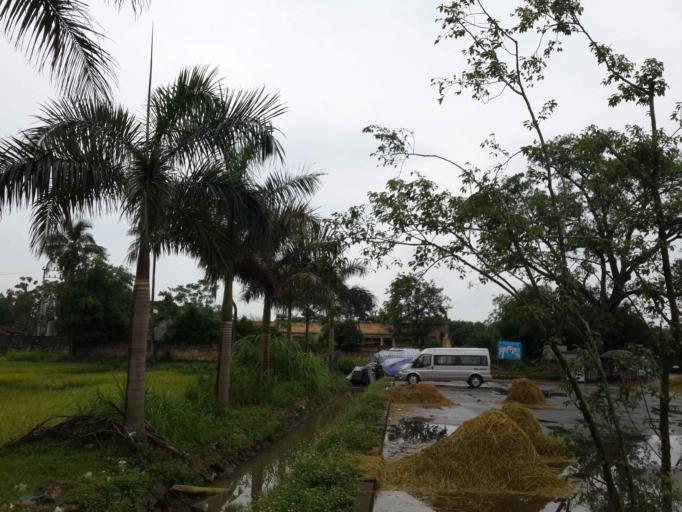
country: VN
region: Ha Noi
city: Son Tay
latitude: 21.1567
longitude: 105.4729
